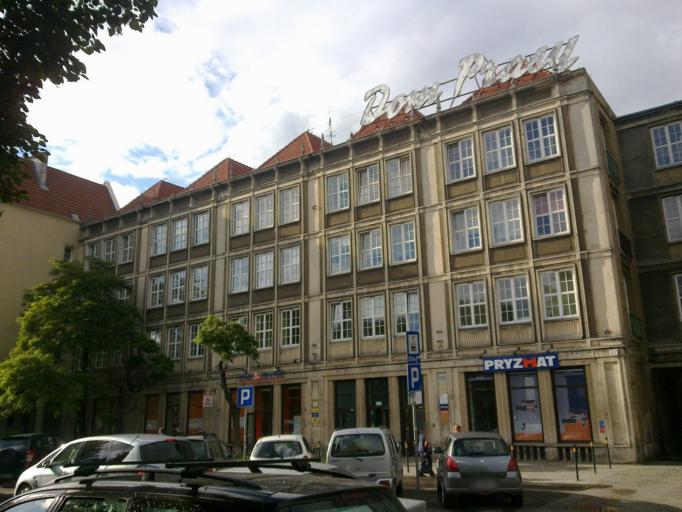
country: PL
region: Pomeranian Voivodeship
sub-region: Gdansk
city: Gdansk
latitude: 54.3524
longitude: 18.6488
